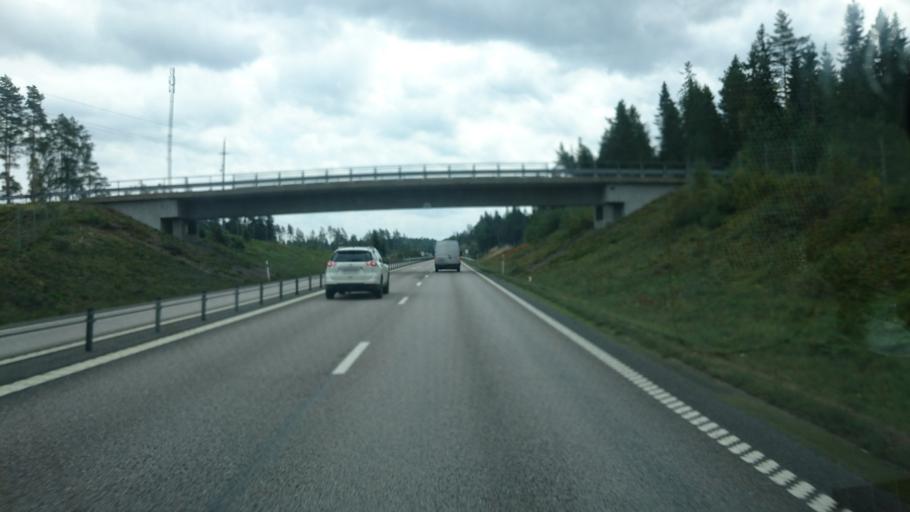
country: SE
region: Vaestra Goetaland
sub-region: Boras Kommun
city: Ganghester
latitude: 57.6639
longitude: 13.0359
